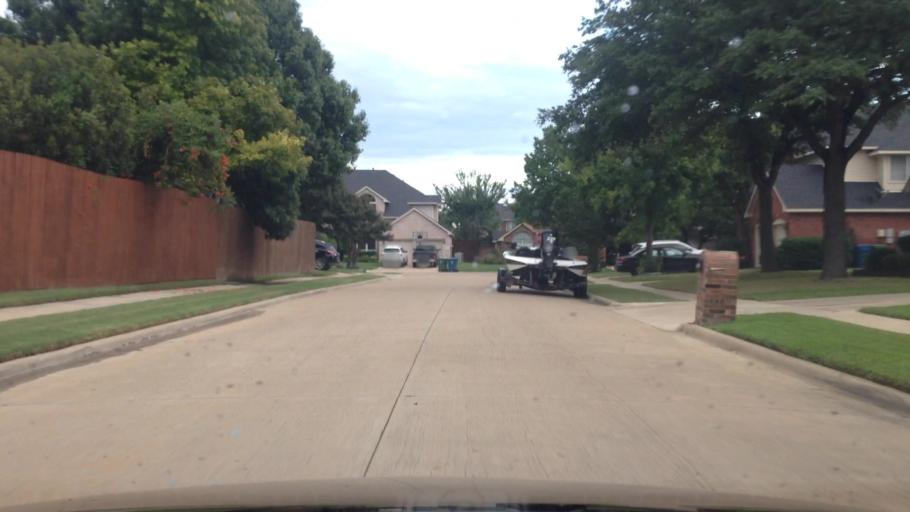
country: US
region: Texas
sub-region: Denton County
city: Flower Mound
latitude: 33.0166
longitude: -97.0543
